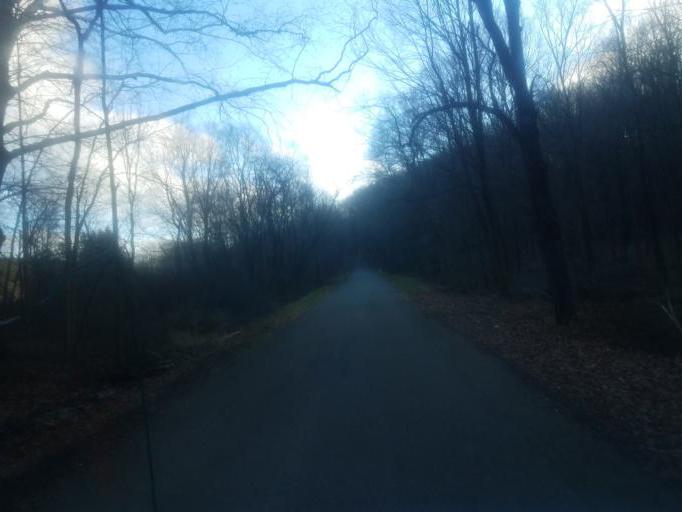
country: US
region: Ohio
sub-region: Sandusky County
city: Bellville
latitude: 40.6003
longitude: -82.3955
